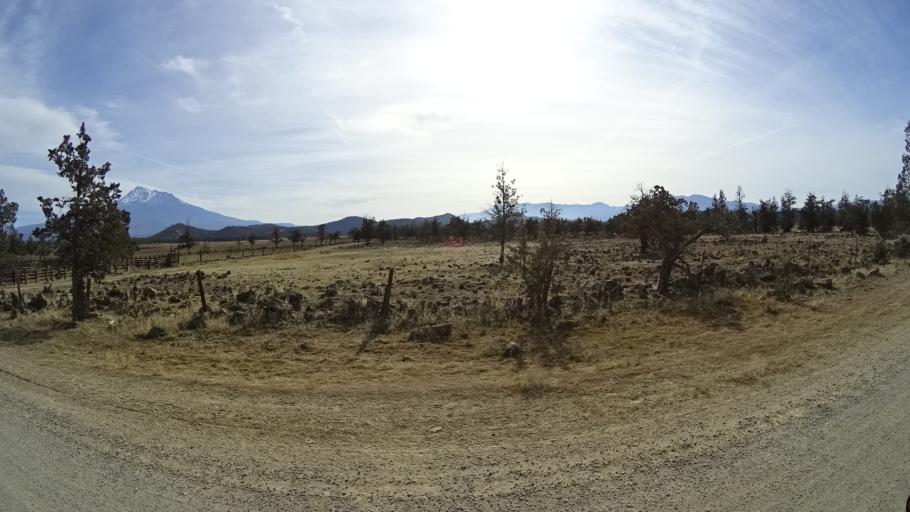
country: US
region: California
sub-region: Siskiyou County
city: Montague
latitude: 41.5953
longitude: -122.4244
